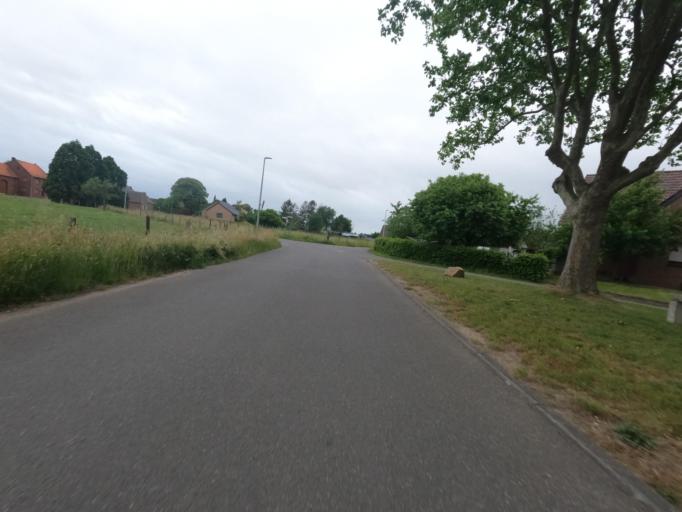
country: DE
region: North Rhine-Westphalia
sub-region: Regierungsbezirk Koln
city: Wassenberg
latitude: 51.1075
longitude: 6.1310
